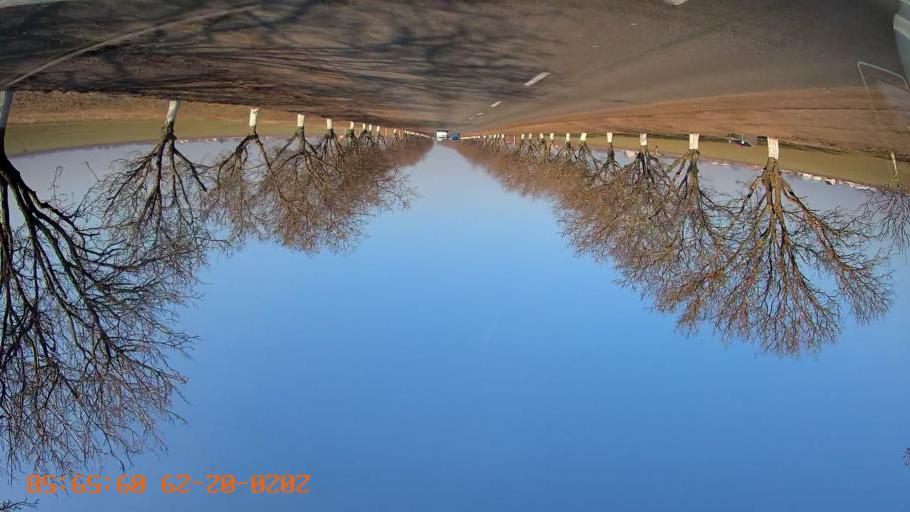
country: MD
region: Telenesti
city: Slobozia
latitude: 46.7628
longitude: 29.6873
